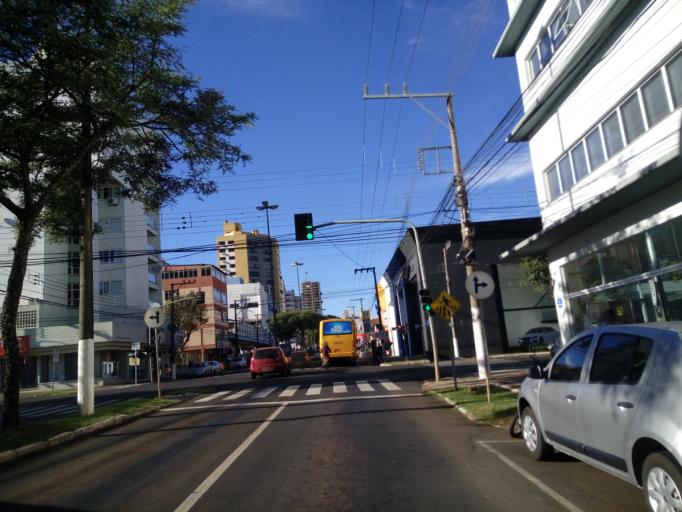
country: BR
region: Santa Catarina
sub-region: Chapeco
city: Chapeco
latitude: -27.1006
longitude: -52.6176
